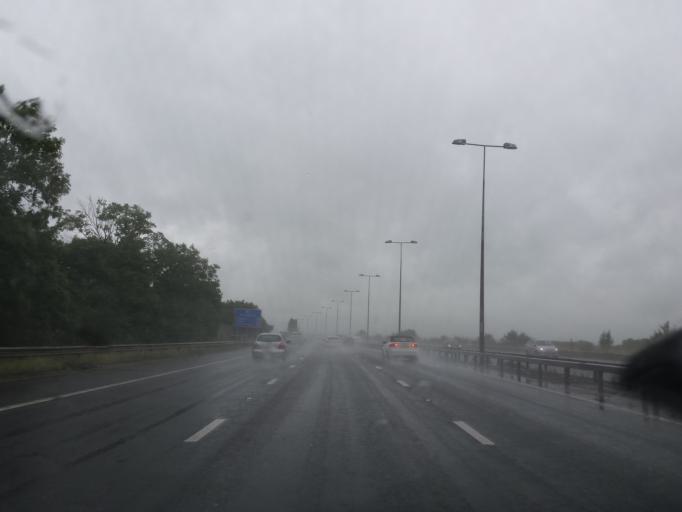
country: GB
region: England
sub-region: Derbyshire
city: Long Eaton
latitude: 52.9073
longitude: -1.3004
